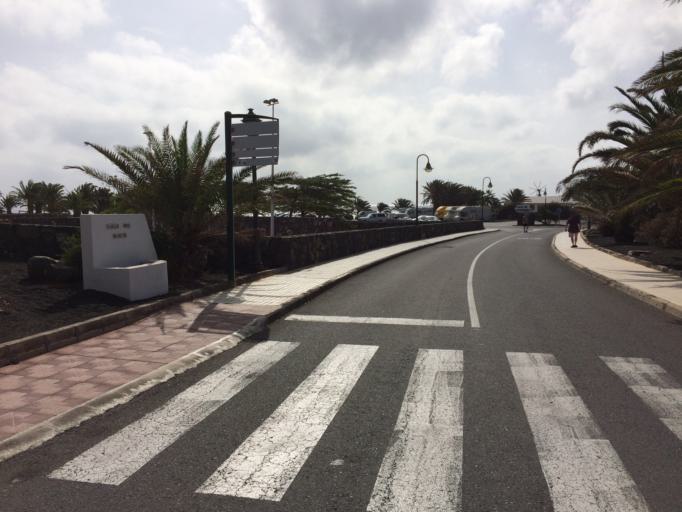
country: ES
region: Canary Islands
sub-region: Provincia de Las Palmas
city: Arrecife
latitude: 29.0023
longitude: -13.4840
